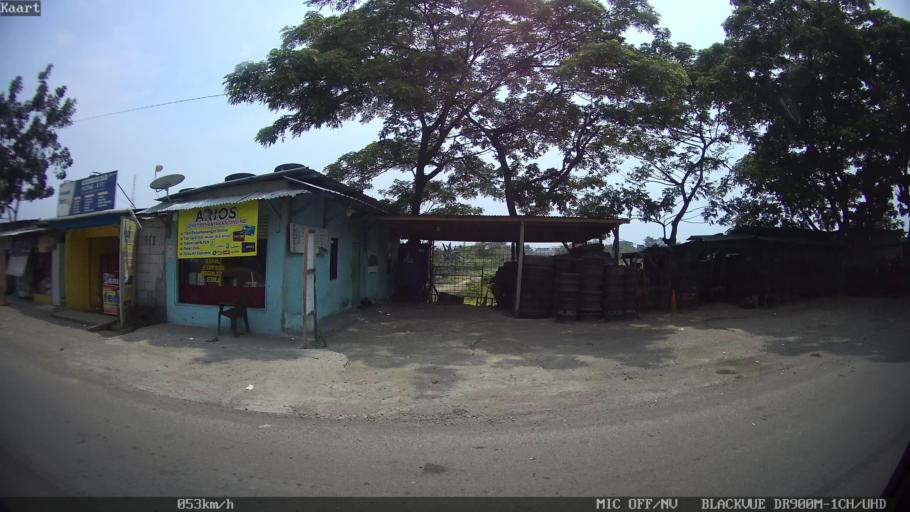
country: ID
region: Banten
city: Curug
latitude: -5.9593
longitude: 106.0058
